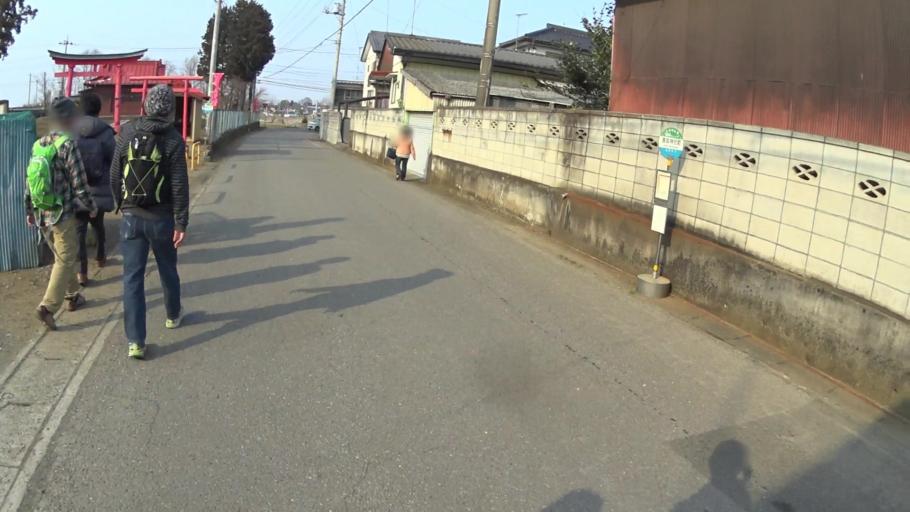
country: JP
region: Ibaraki
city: Koga
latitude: 36.1821
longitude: 139.6996
